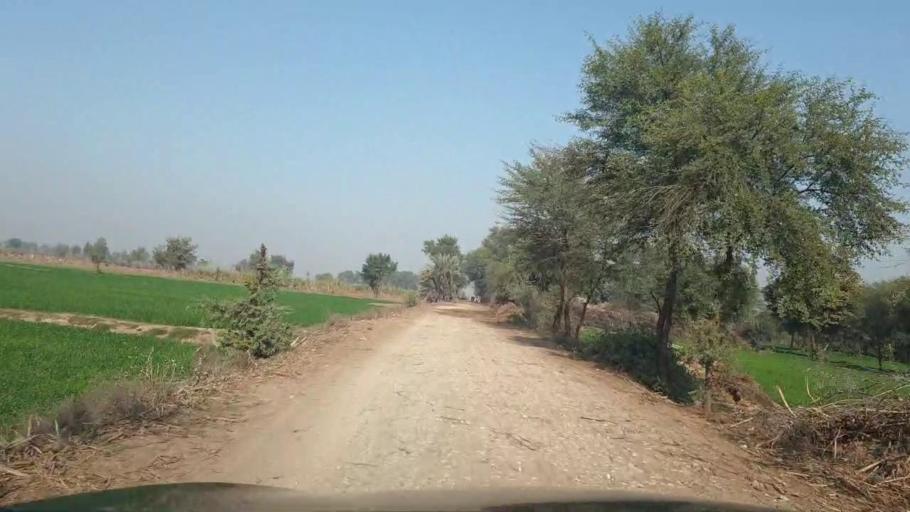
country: PK
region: Sindh
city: Ubauro
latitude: 28.1202
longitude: 69.7509
